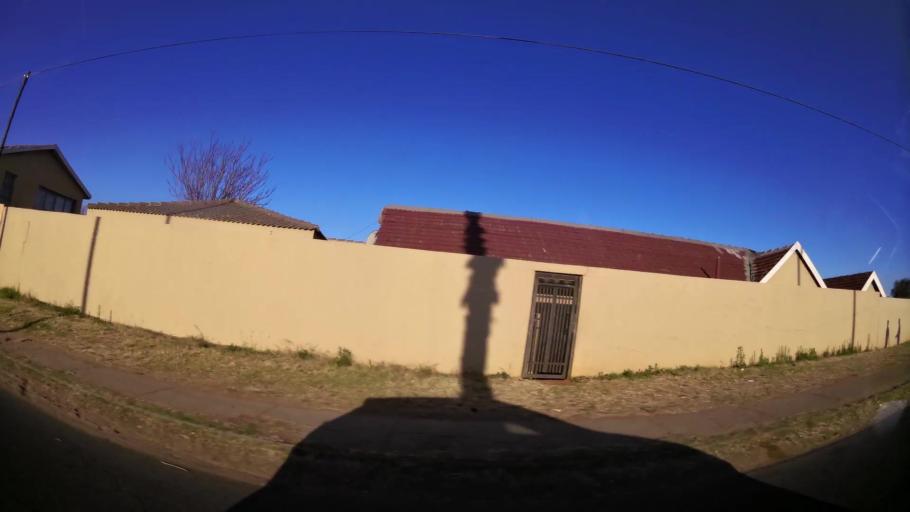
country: ZA
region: Gauteng
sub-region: City of Johannesburg Metropolitan Municipality
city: Roodepoort
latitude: -26.1623
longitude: 27.8727
